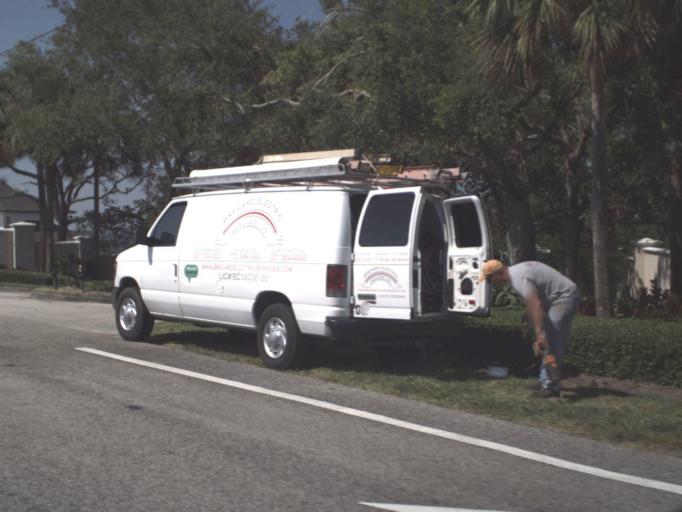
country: US
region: Florida
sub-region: Brevard County
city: South Patrick Shores
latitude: 28.2231
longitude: -80.6702
